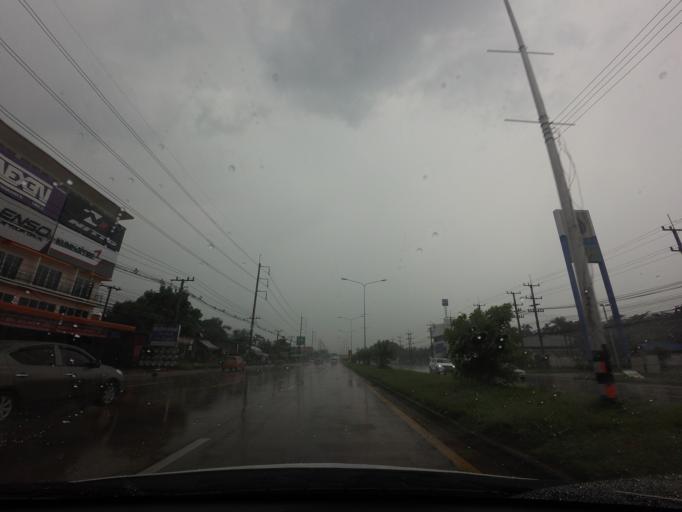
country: TH
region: Nakhon Pathom
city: Sam Phran
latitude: 13.7376
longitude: 100.2427
